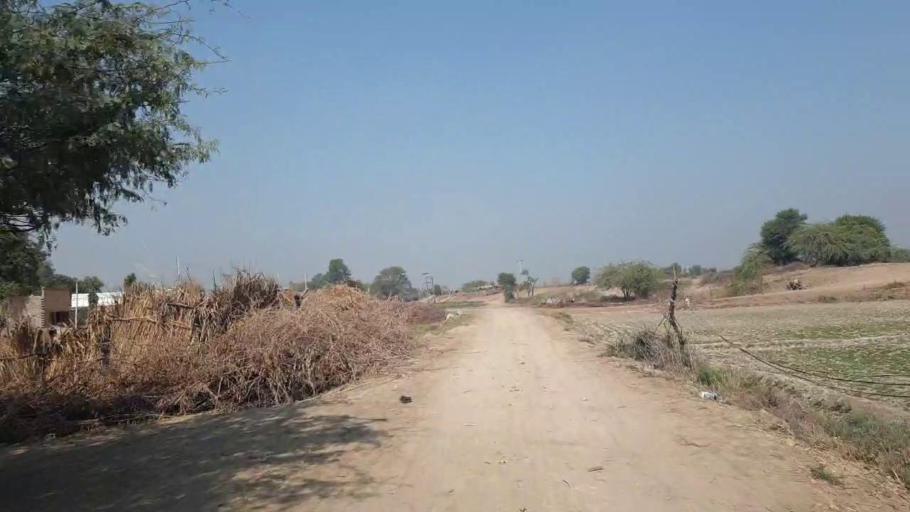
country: PK
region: Sindh
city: Chambar
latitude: 25.3529
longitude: 68.8470
